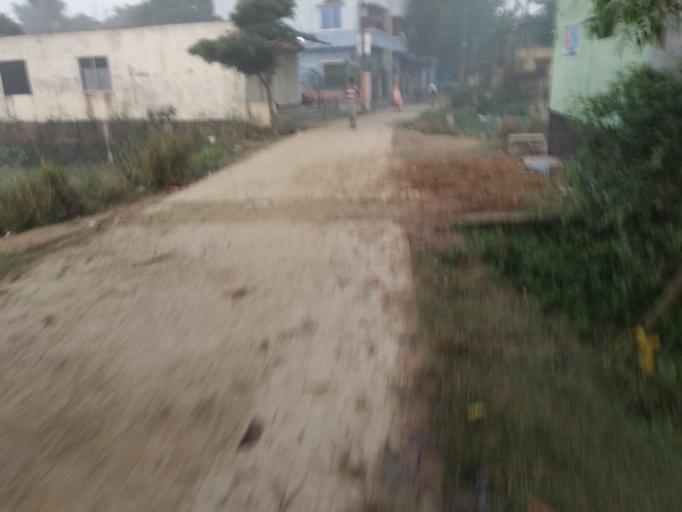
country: BD
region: Dhaka
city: Tungi
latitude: 23.8567
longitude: 90.4360
